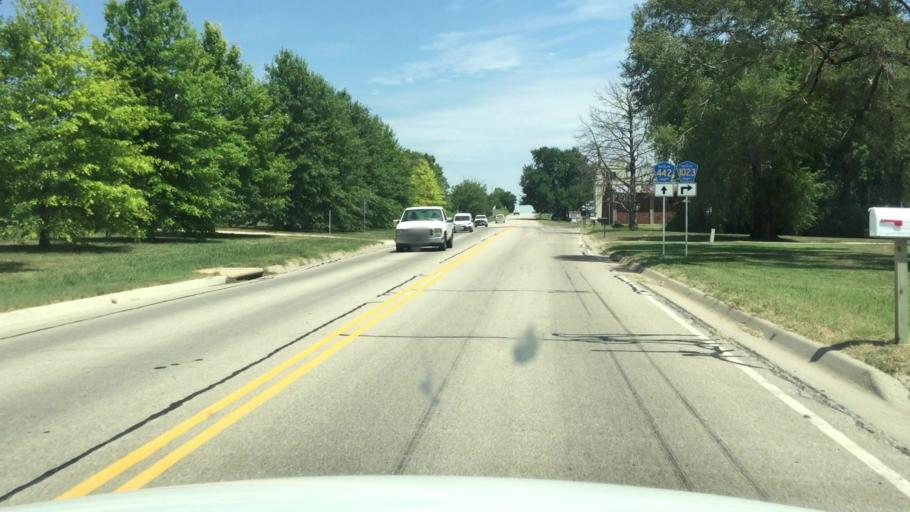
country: US
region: Kansas
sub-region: Osage County
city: Overbrook
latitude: 38.9712
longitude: -95.4577
